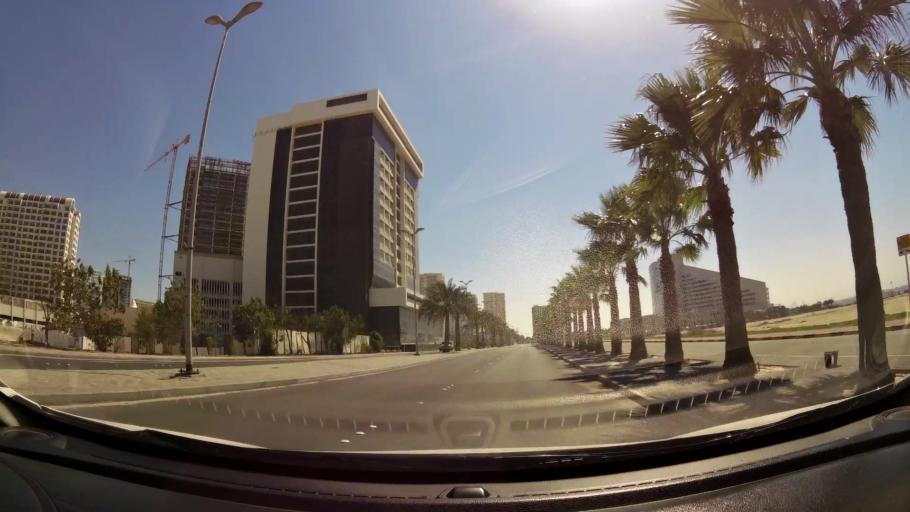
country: BH
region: Muharraq
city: Al Hadd
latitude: 26.2929
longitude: 50.6624
